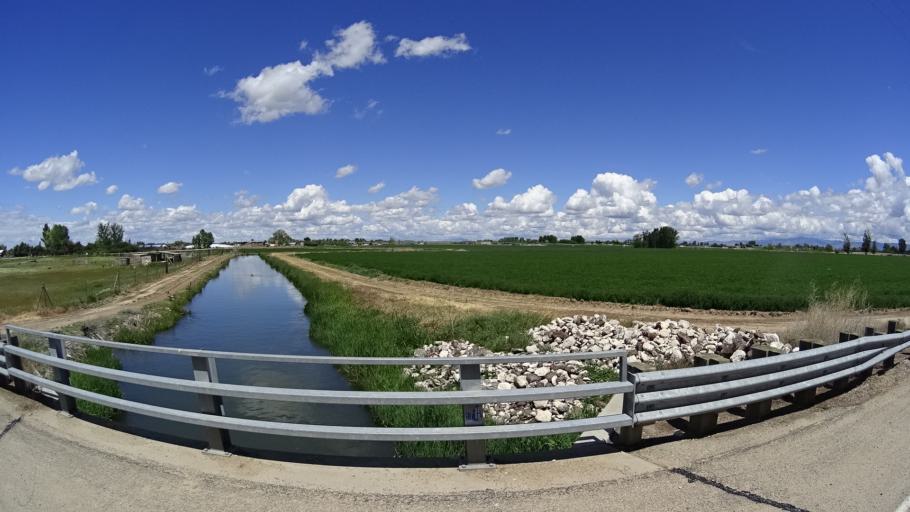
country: US
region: Idaho
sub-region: Ada County
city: Kuna
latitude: 43.5465
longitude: -116.4511
